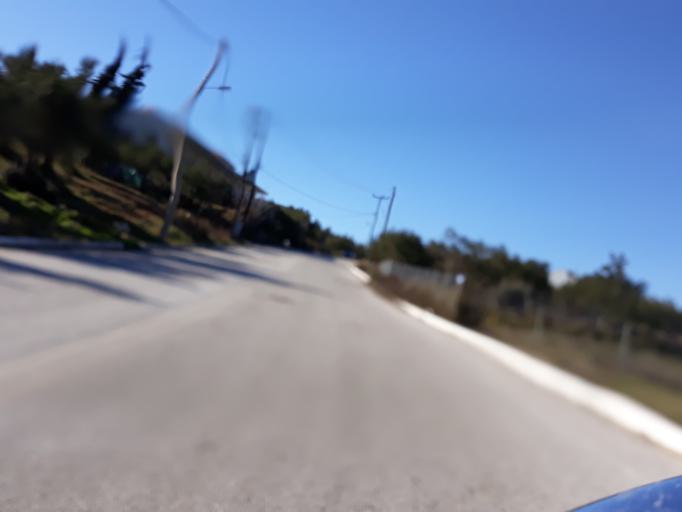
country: GR
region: Attica
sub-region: Nomarchia Dytikis Attikis
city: Fyli
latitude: 38.1071
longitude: 23.6790
